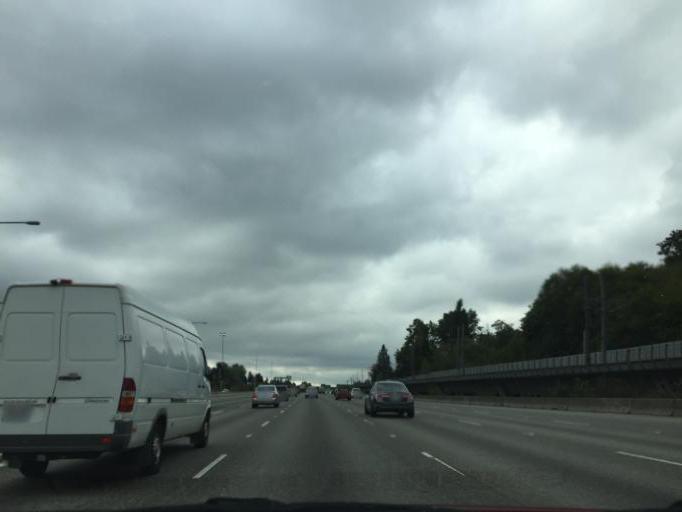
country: US
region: Washington
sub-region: King County
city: Tukwila
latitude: 47.4787
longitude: -122.2721
